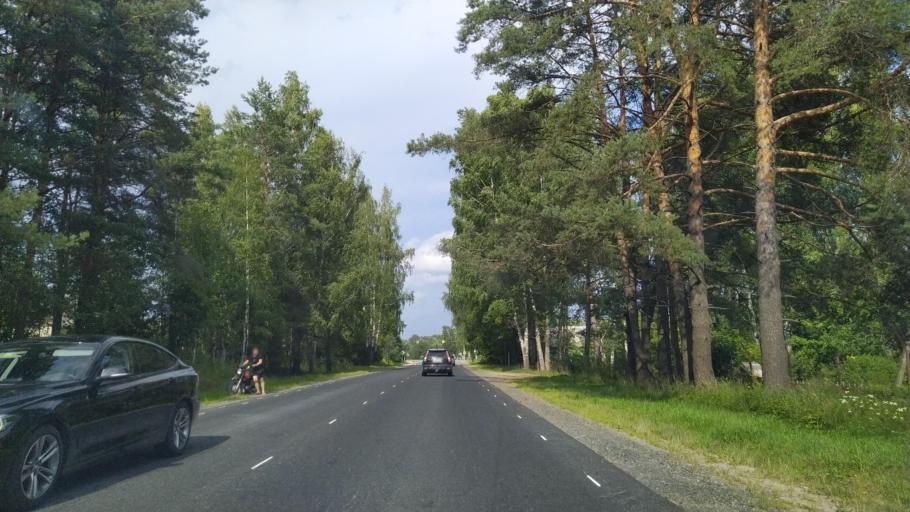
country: RU
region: Pskov
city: Porkhov
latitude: 57.8481
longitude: 29.5480
